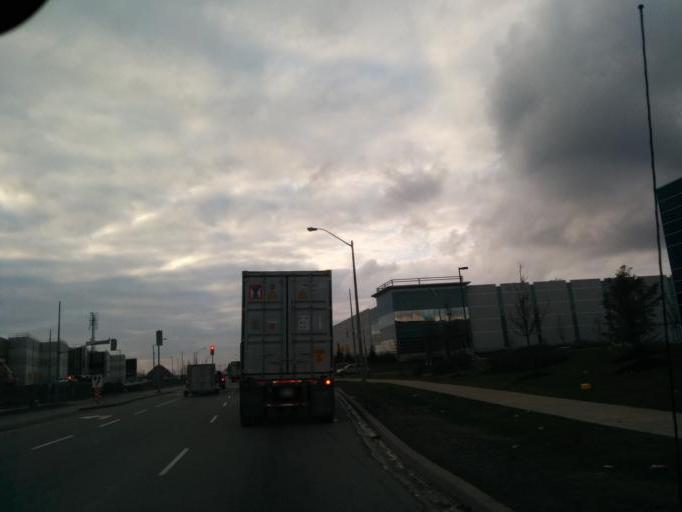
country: CA
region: Ontario
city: Etobicoke
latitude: 43.7752
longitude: -79.6429
